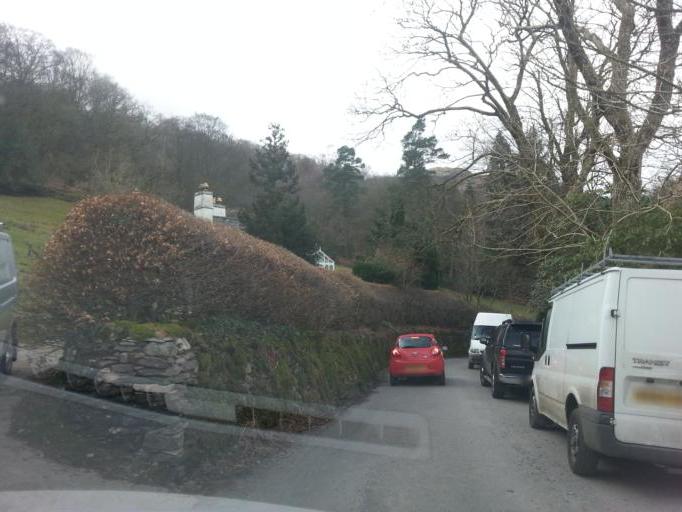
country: GB
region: England
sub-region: Cumbria
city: Ambleside
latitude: 54.4462
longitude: -3.0255
